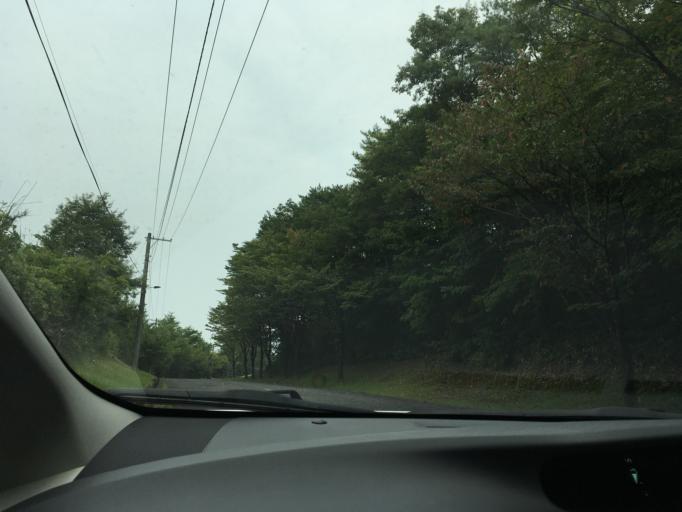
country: JP
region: Iwate
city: Ichinoseki
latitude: 38.8782
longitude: 141.0735
